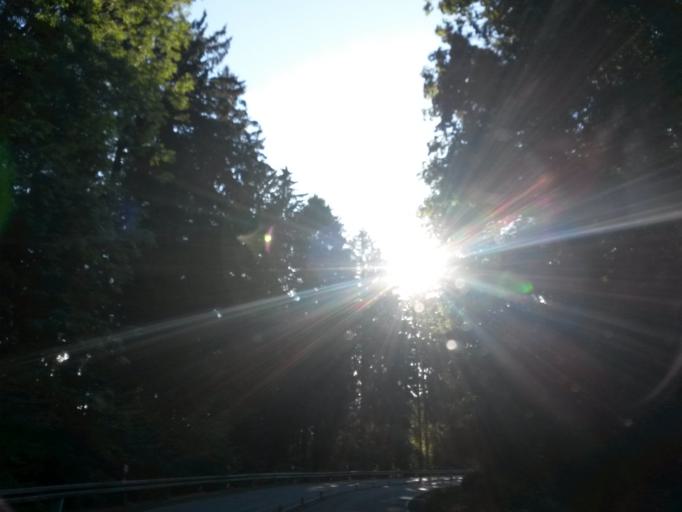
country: DE
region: North Rhine-Westphalia
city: Meinerzhagen
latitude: 51.0920
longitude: 7.6415
